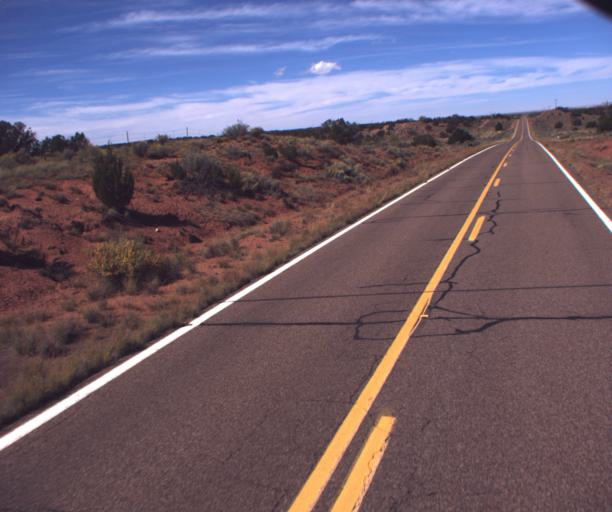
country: US
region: Arizona
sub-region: Apache County
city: Saint Johns
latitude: 34.5962
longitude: -109.6496
